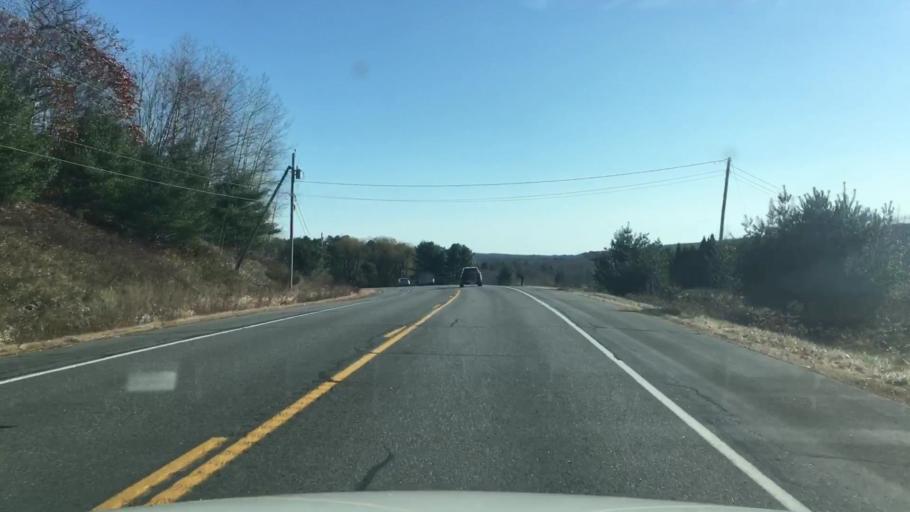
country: US
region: Maine
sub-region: Knox County
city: Union
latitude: 44.2176
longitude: -69.3152
